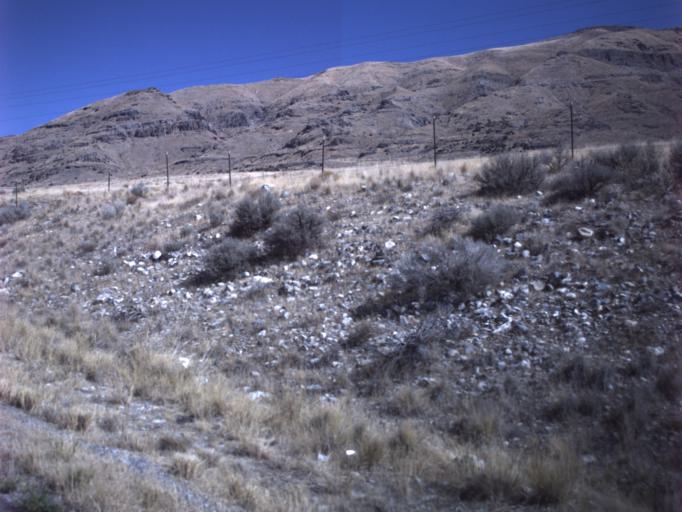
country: US
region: Utah
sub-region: Tooele County
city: Grantsville
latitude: 40.6680
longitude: -112.6749
